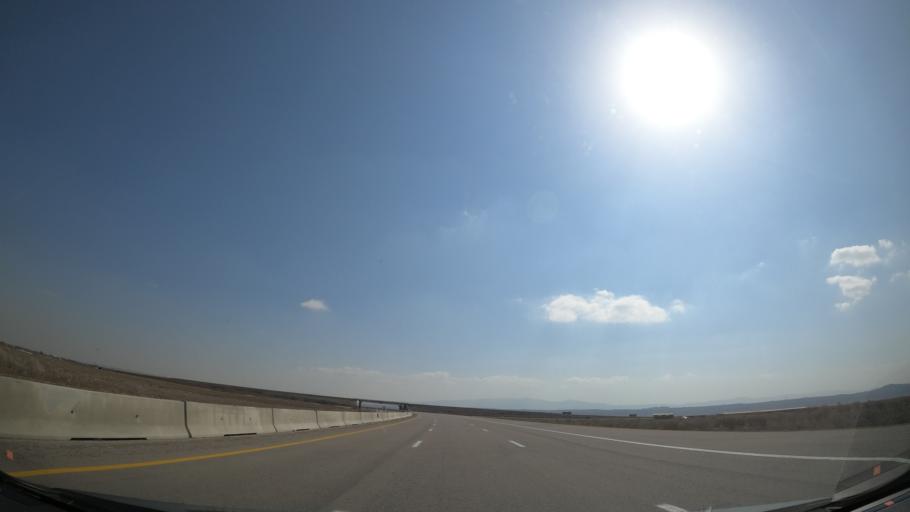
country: IR
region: Alborz
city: Nazarabad
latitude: 35.8458
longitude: 50.4824
